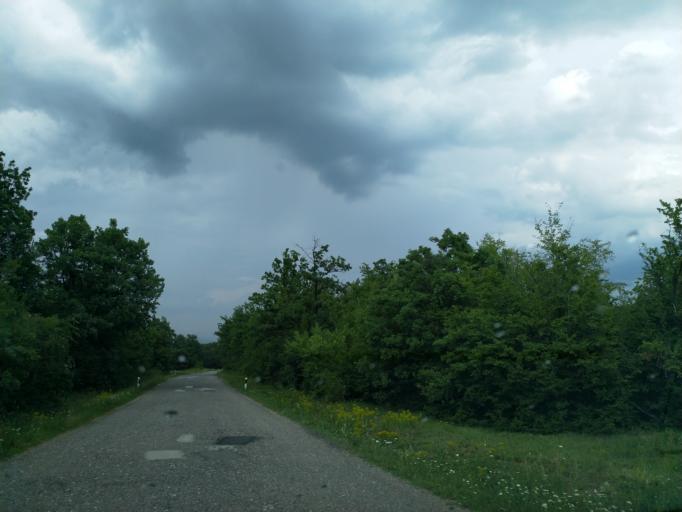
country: RS
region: Central Serbia
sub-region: Zajecarski Okrug
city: Boljevac
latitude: 43.9651
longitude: 21.9658
